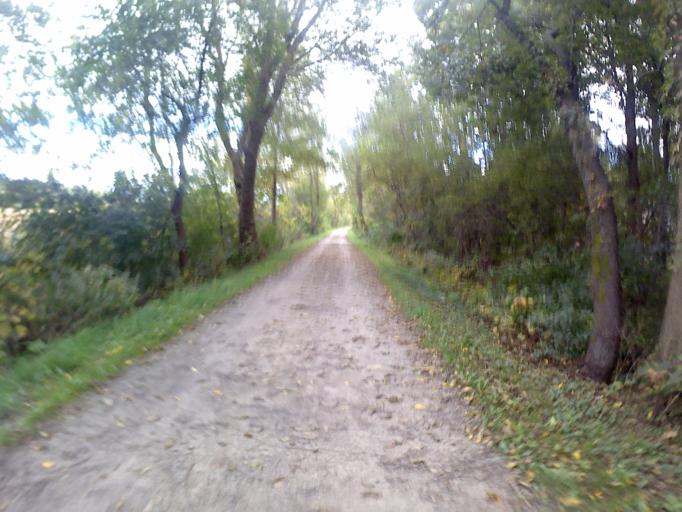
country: US
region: Illinois
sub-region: DuPage County
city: West Chicago
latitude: 41.9021
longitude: -88.1808
